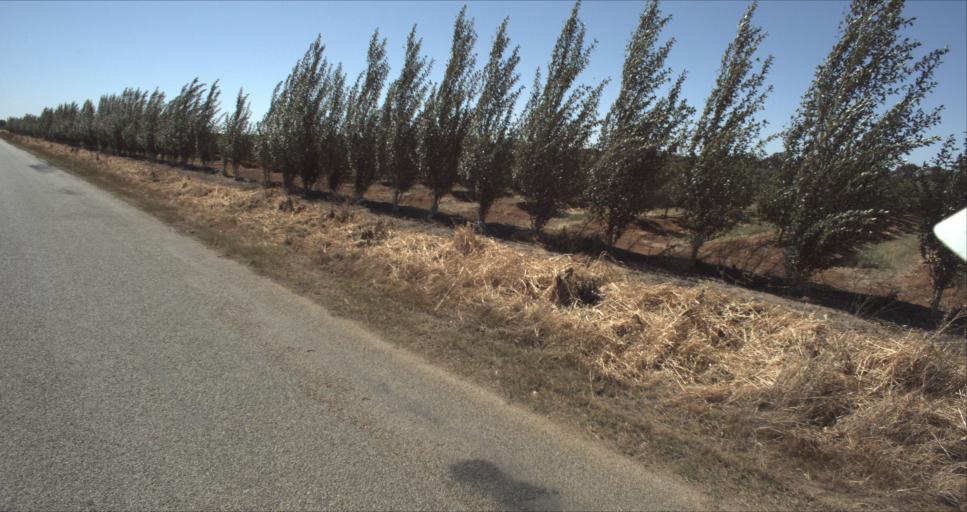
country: AU
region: New South Wales
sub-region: Leeton
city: Leeton
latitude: -34.5462
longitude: 146.3687
